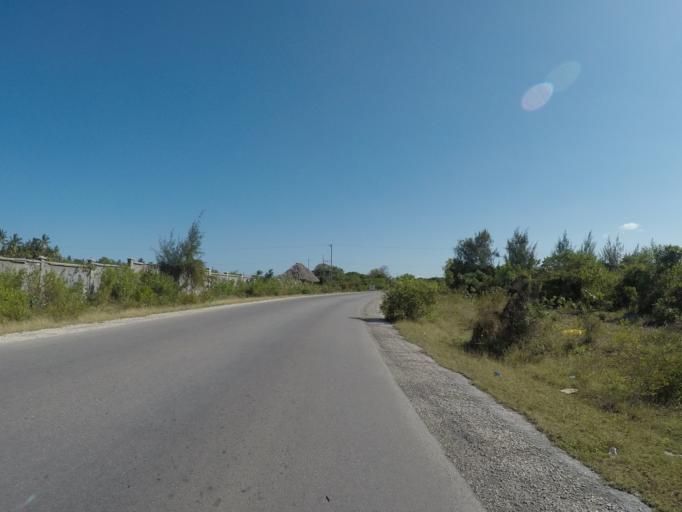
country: TZ
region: Zanzibar Central/South
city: Nganane
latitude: -6.2002
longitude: 39.5314
